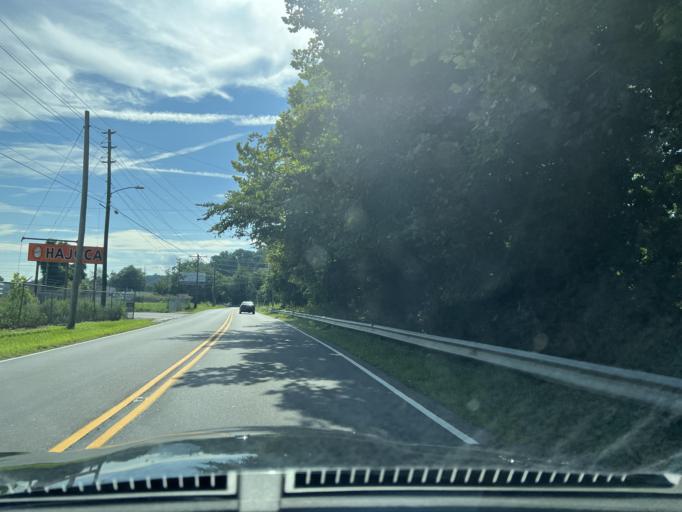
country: US
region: North Carolina
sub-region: Buncombe County
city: Asheville
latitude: 35.5722
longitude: -82.5329
